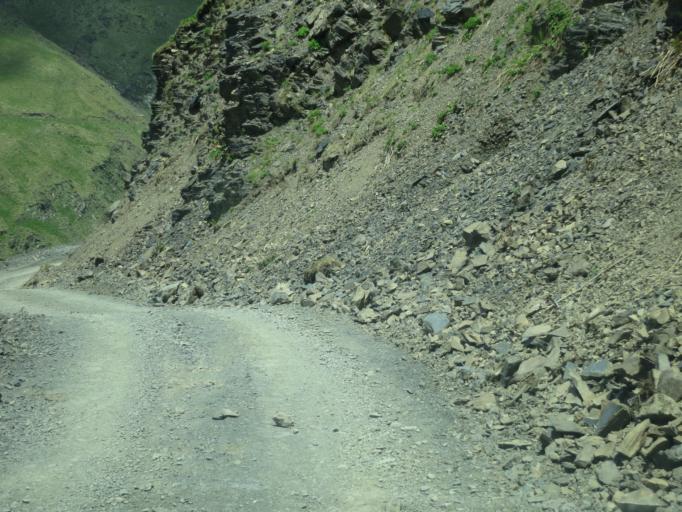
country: GE
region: Kakheti
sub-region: Telavi
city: Telavi
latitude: 42.2720
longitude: 45.4921
